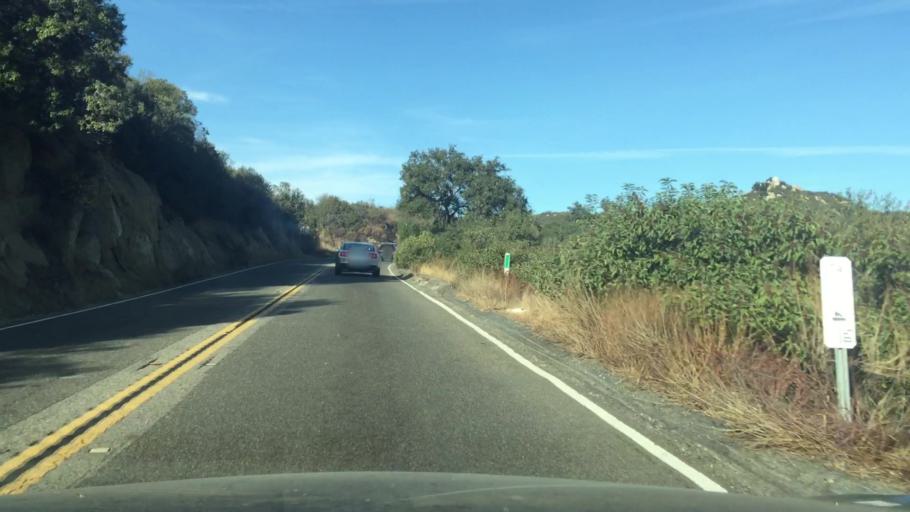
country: US
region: California
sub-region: Riverside County
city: Lakeland Village
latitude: 33.6271
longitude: -117.4260
